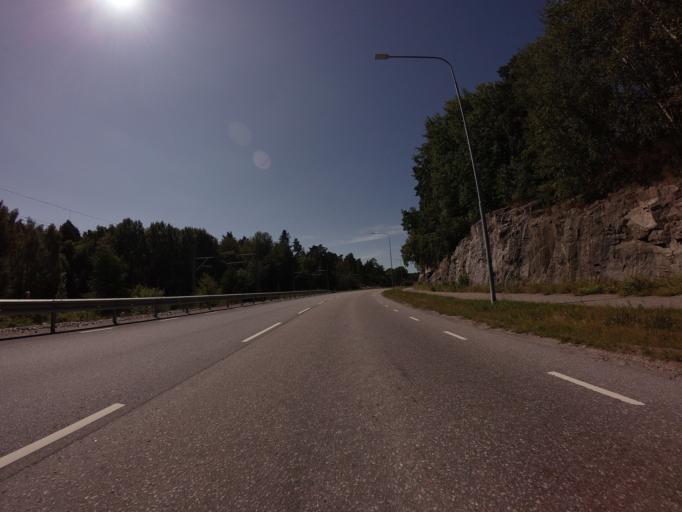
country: SE
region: Stockholm
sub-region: Lidingo
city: Brevik
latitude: 59.3542
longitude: 18.2210
